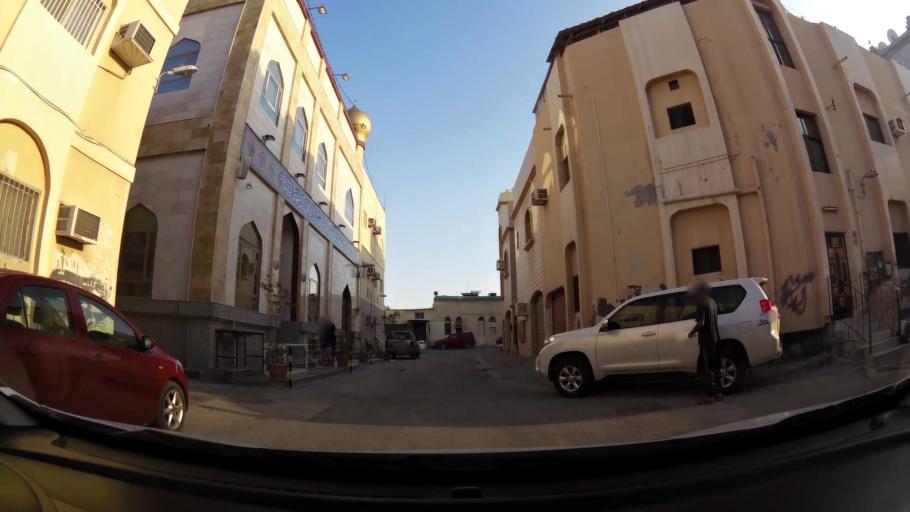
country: BH
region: Manama
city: Jidd Hafs
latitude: 26.2247
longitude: 50.5582
